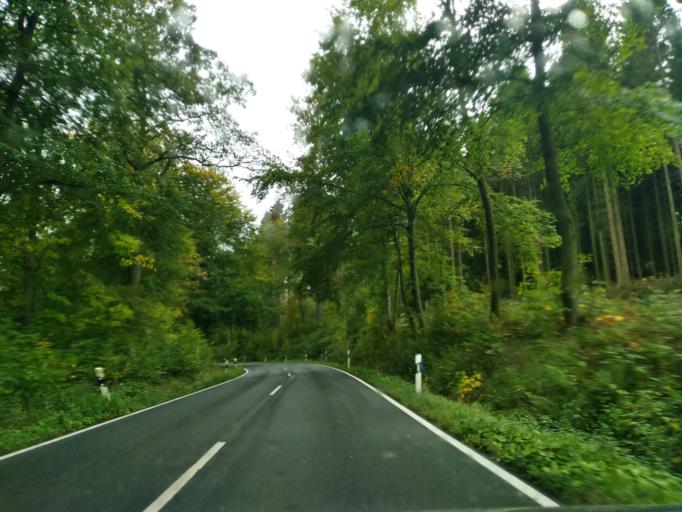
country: DE
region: North Rhine-Westphalia
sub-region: Regierungsbezirk Koln
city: Bad Honnef
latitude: 50.6531
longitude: 7.2894
